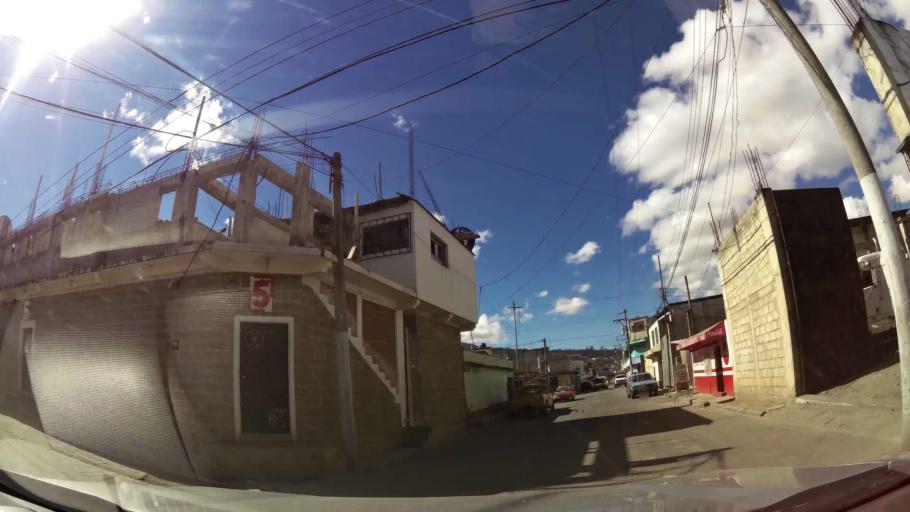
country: GT
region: Quetzaltenango
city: Quetzaltenango
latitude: 14.8421
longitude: -91.5058
